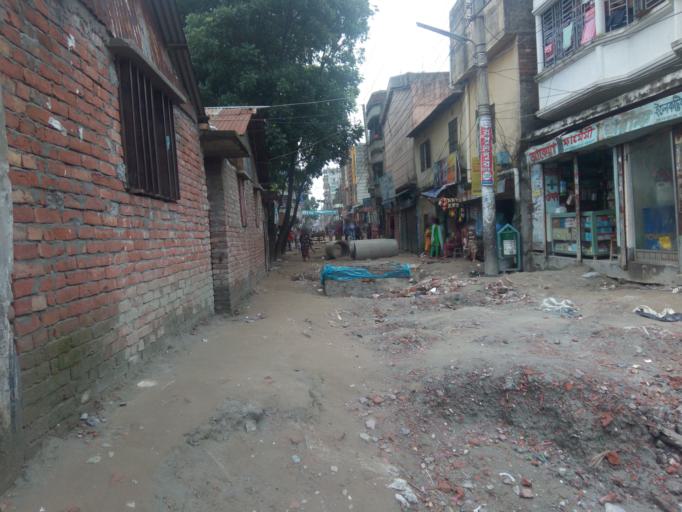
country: BD
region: Dhaka
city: Azimpur
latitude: 23.7181
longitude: 90.3742
